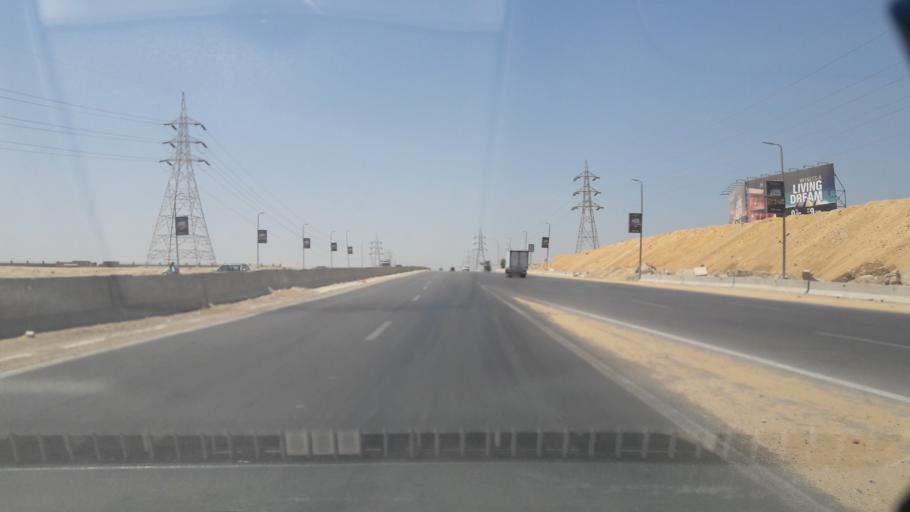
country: EG
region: Al Jizah
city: Al Jizah
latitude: 30.0029
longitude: 31.0895
